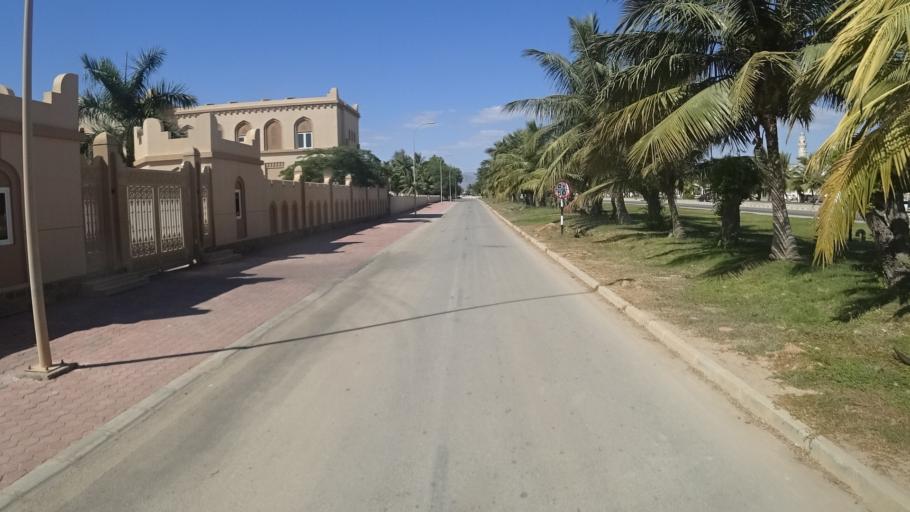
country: OM
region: Zufar
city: Salalah
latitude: 17.0027
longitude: 54.0639
